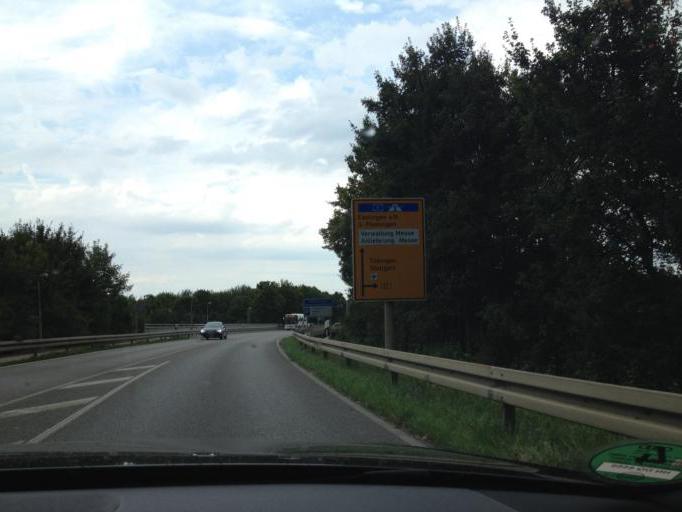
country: DE
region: Baden-Wuerttemberg
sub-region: Regierungsbezirk Stuttgart
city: Leinfelden-Echterdingen
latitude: 48.6909
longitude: 9.1770
